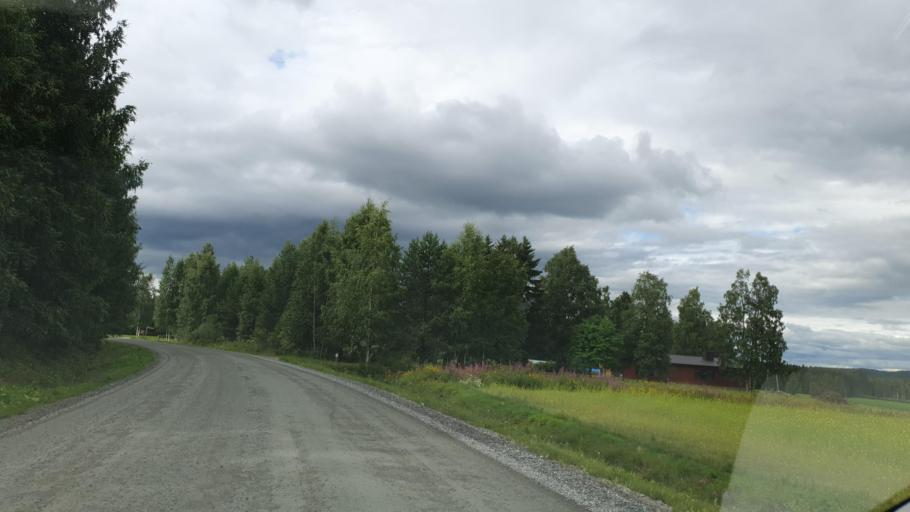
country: FI
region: Northern Savo
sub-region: Ylae-Savo
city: Iisalmi
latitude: 63.5358
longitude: 27.0854
